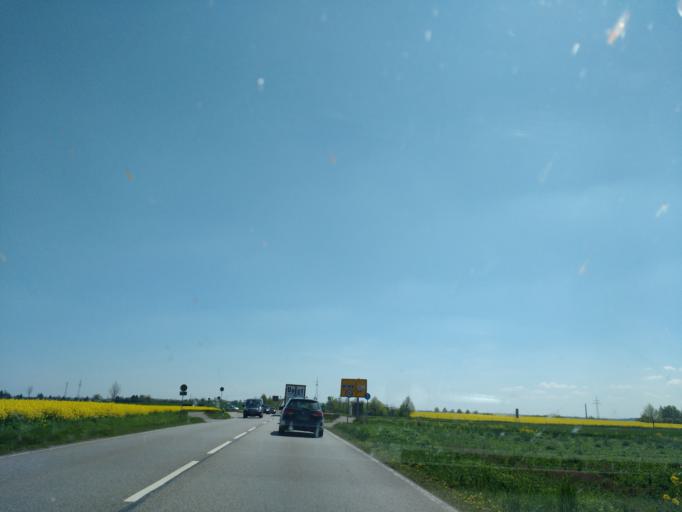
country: DE
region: Saxony-Anhalt
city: Theissen
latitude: 51.0802
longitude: 12.1129
